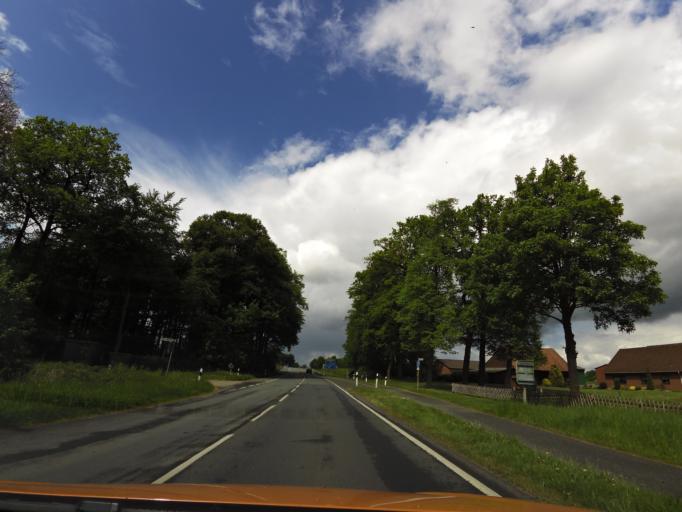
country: DE
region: Lower Saxony
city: Ganderkesee
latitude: 53.0533
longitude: 8.5341
